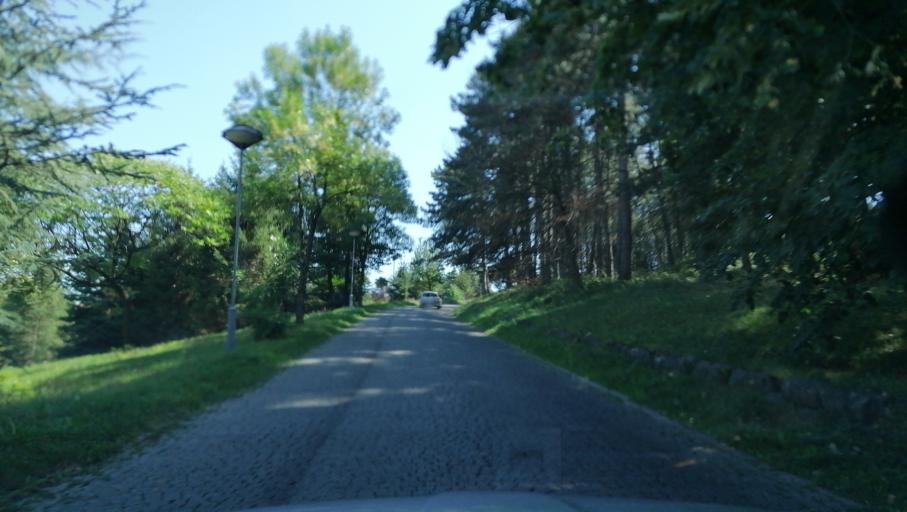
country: RS
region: Central Serbia
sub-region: Kolubarski Okrug
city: Valjevo
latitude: 44.2654
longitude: 19.8799
